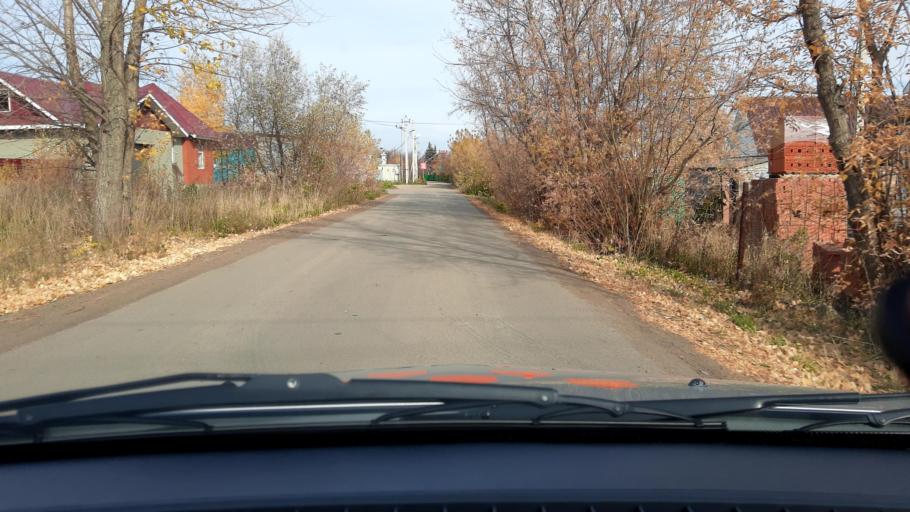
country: RU
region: Bashkortostan
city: Mikhaylovka
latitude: 54.7889
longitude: 55.8302
